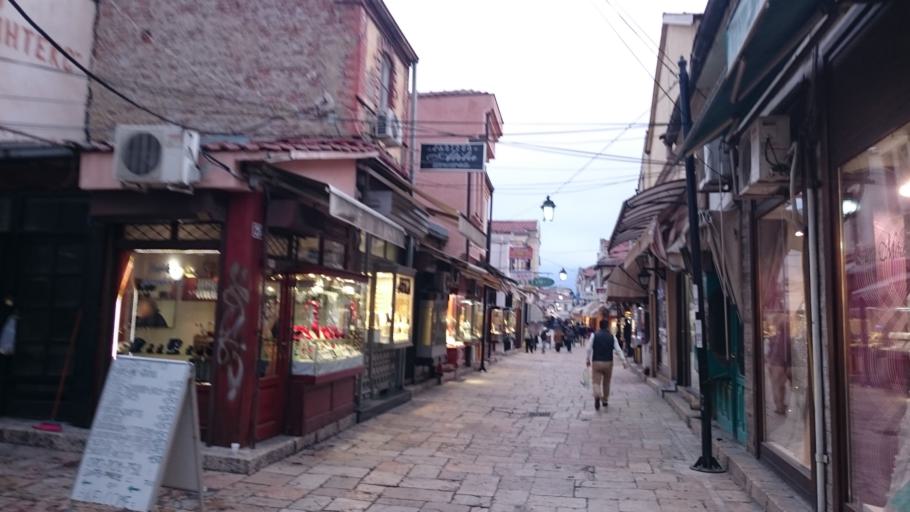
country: MK
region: Karpos
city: Skopje
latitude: 42.0011
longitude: 21.4370
